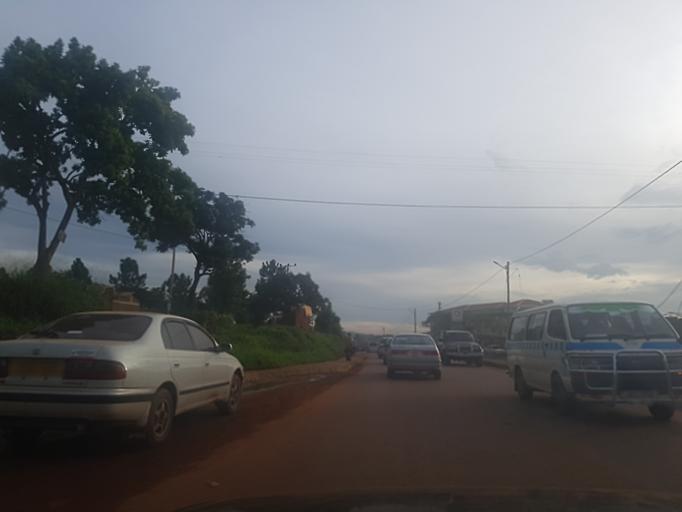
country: UG
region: Central Region
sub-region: Wakiso District
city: Bweyogerere
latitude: 0.3903
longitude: 32.6575
